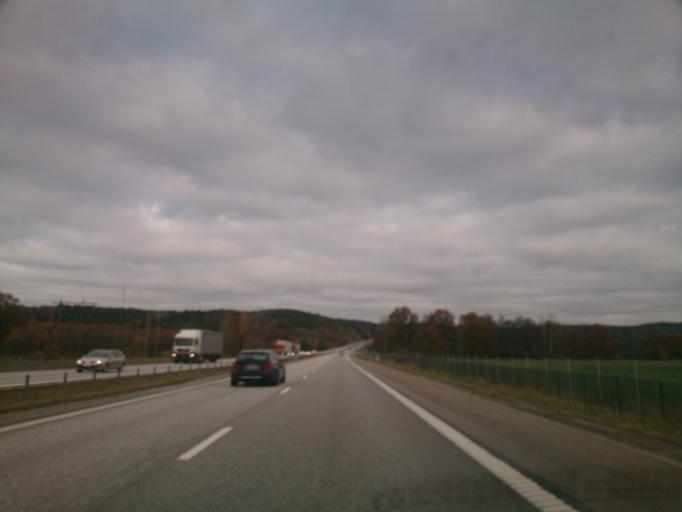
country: SE
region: OEstergoetland
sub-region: Norrkopings Kommun
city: Jursla
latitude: 58.6599
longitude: 16.1969
